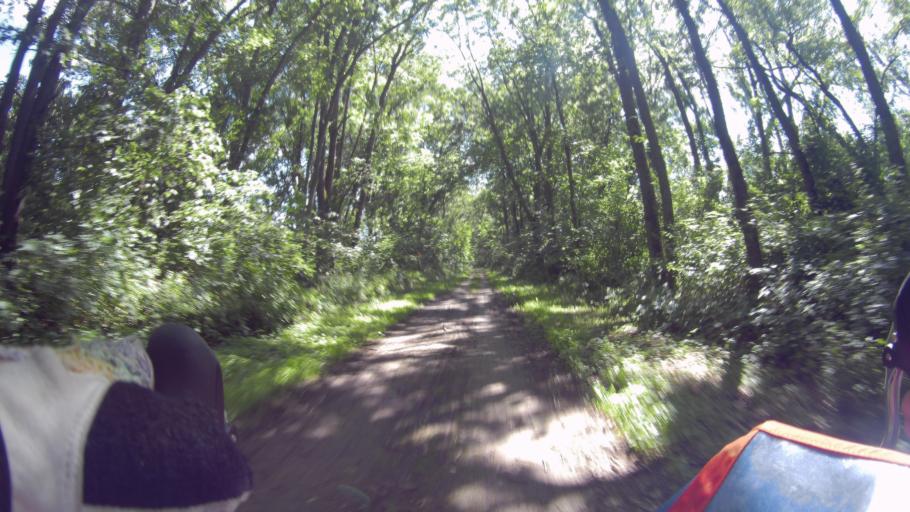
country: US
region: Wisconsin
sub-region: Dane County
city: Fitchburg
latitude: 42.9268
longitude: -89.5073
